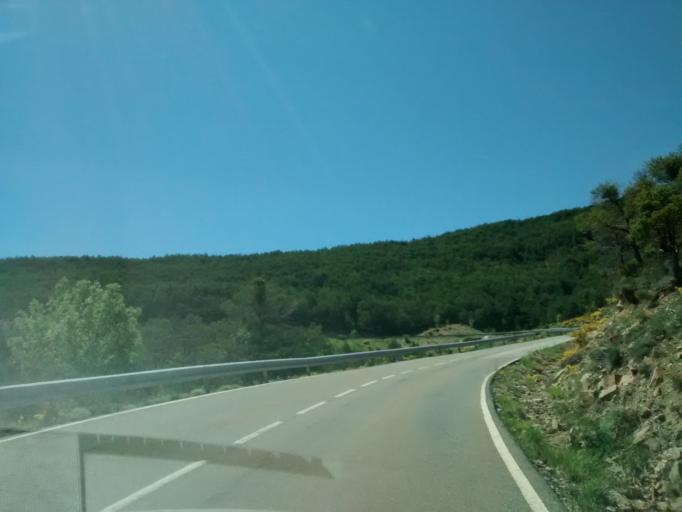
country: ES
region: Aragon
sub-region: Provincia de Huesca
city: Borau
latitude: 42.6539
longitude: -0.5712
